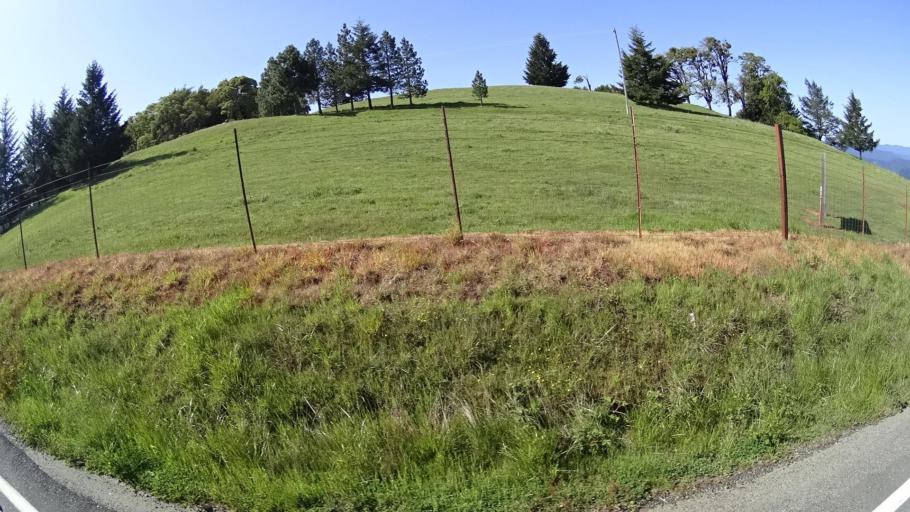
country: US
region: California
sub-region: Humboldt County
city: Redway
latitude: 40.1115
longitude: -123.7537
